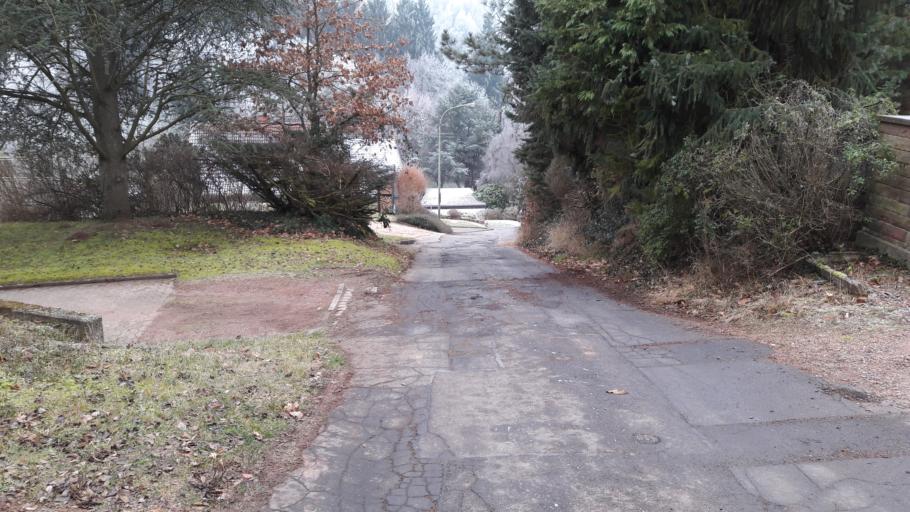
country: DE
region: Saarland
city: Ottweiler
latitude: 49.3980
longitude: 7.1597
